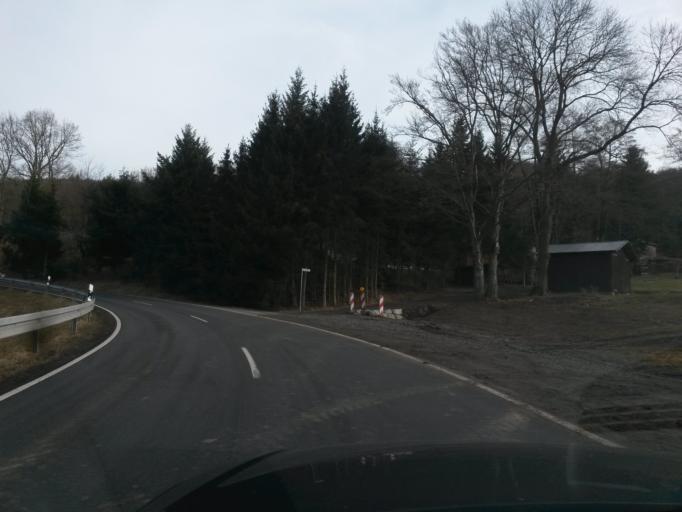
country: DE
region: Hesse
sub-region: Regierungsbezirk Kassel
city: Hilders
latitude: 50.5727
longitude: 10.0164
